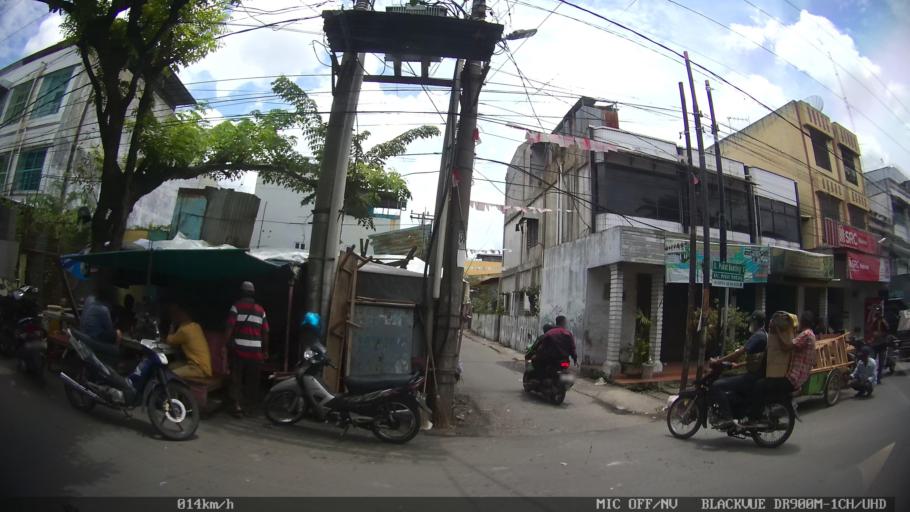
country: ID
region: North Sumatra
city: Medan
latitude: 3.5950
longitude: 98.7117
